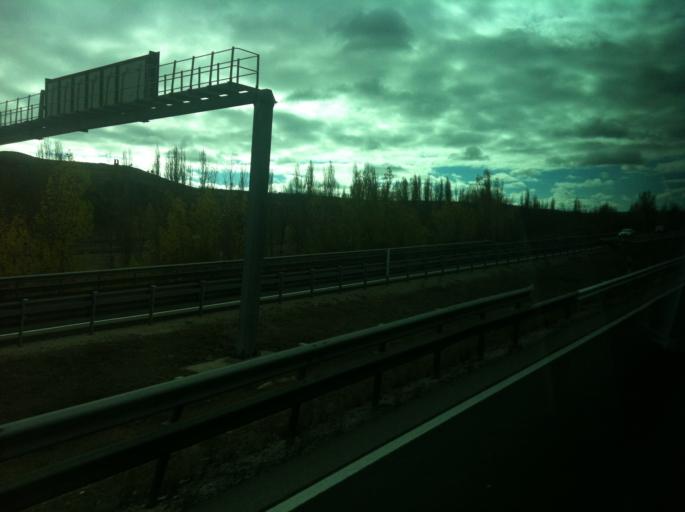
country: ES
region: Castille and Leon
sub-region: Provincia de Burgos
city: Pradanos de Bureba
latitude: 42.5228
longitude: -3.3382
